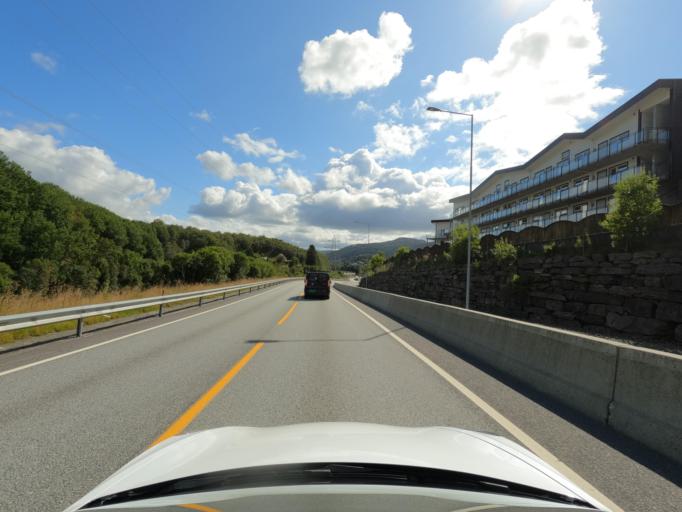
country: NO
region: Hordaland
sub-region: Bergen
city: Hylkje
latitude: 60.4746
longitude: 5.3212
